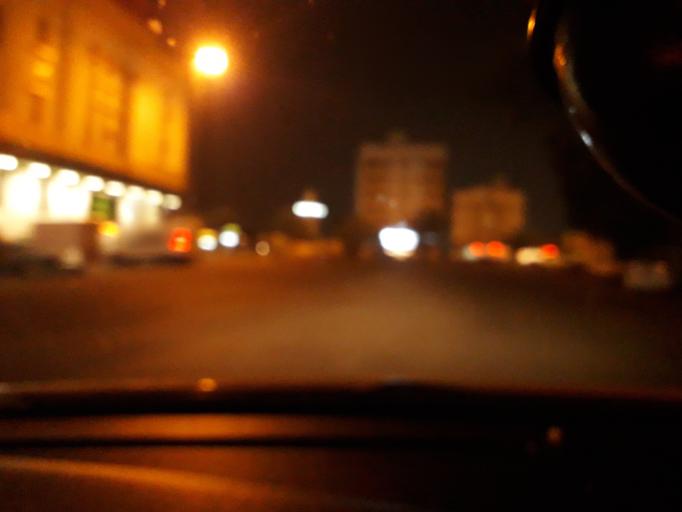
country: SA
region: Al Madinah al Munawwarah
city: Medina
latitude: 24.4586
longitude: 39.5863
